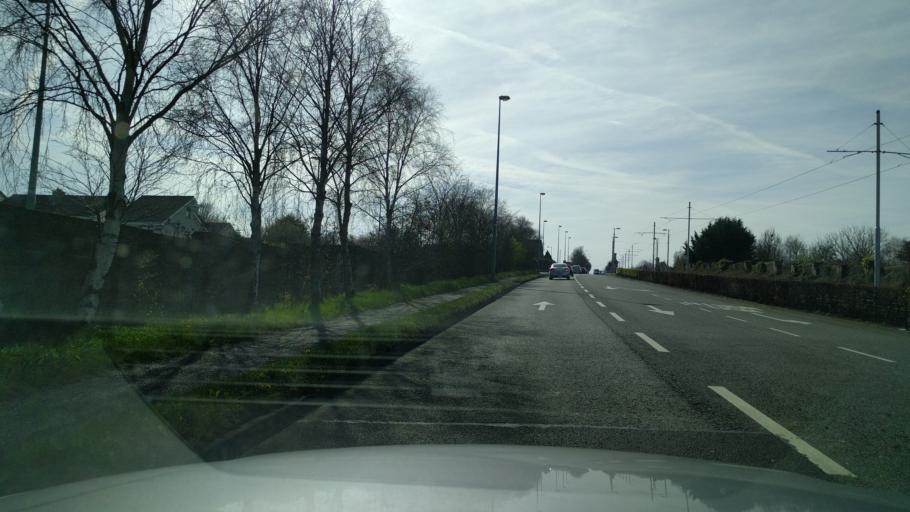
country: IE
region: Leinster
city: Tallaght
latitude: 53.3043
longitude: -6.3630
